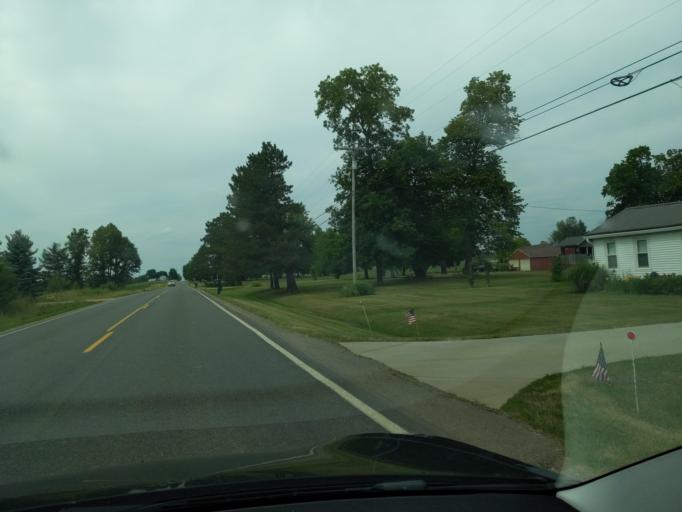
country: US
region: Michigan
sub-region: Clinton County
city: DeWitt
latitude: 42.8482
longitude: -84.6025
